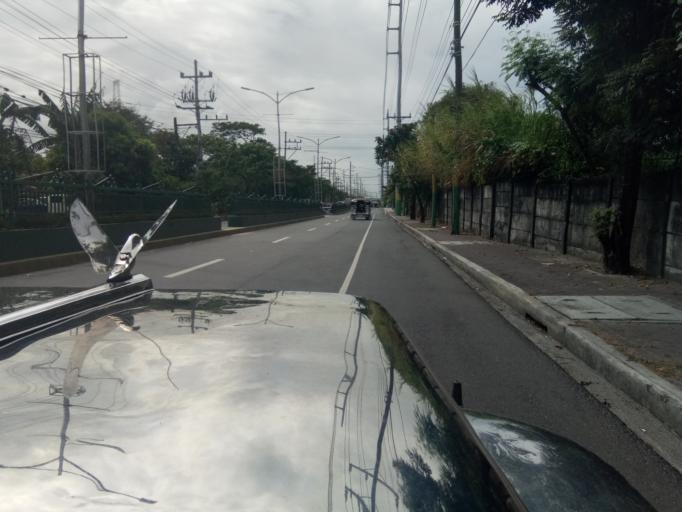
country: PH
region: Calabarzon
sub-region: Province of Cavite
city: Dasmarinas
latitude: 14.3088
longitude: 120.9514
